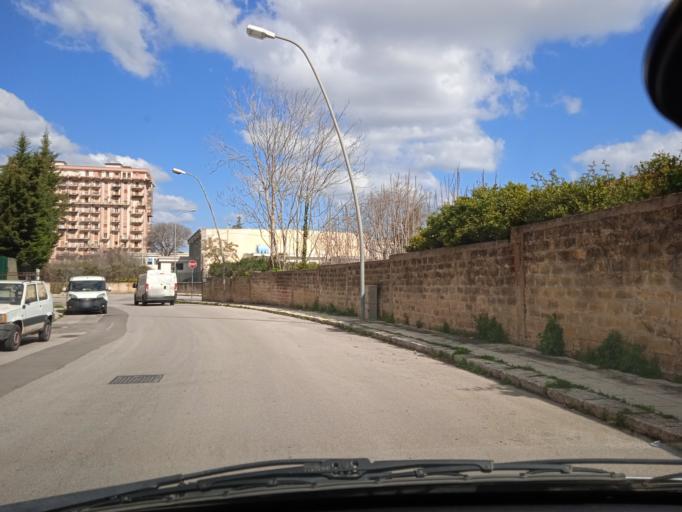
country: IT
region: Sicily
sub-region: Palermo
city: Ciaculli
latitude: 38.0821
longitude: 13.3616
